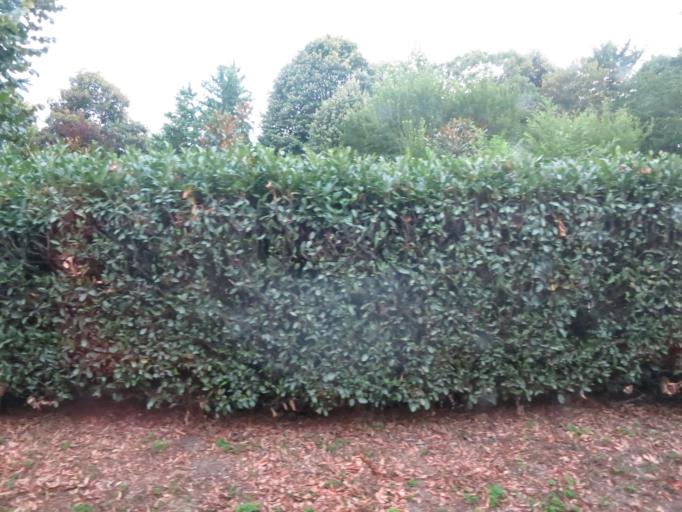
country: IT
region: Lombardy
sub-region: Provincia di Como
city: Novedrate
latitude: 45.6933
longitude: 9.1137
